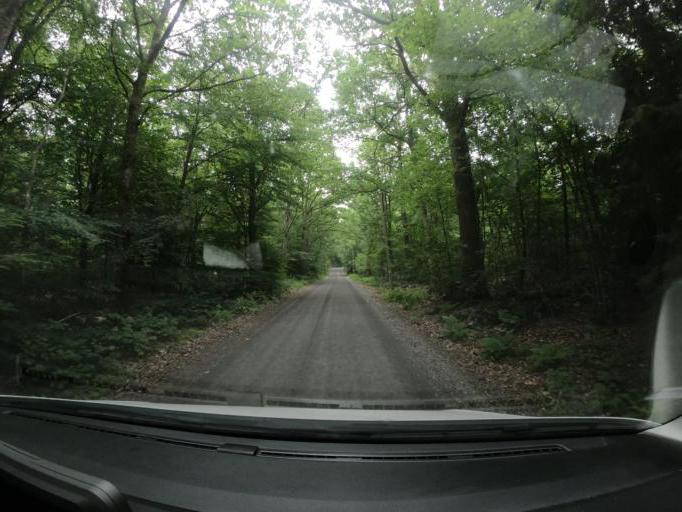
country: SE
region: Skane
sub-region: Hoors Kommun
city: Hoeoer
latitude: 55.9831
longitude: 13.4963
